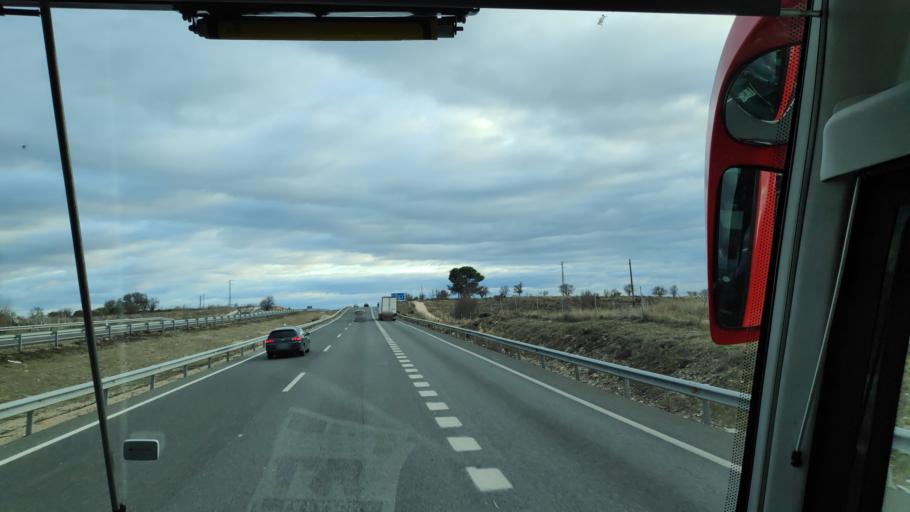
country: ES
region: Madrid
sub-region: Provincia de Madrid
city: Villarejo de Salvanes
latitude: 40.1844
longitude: -3.2978
